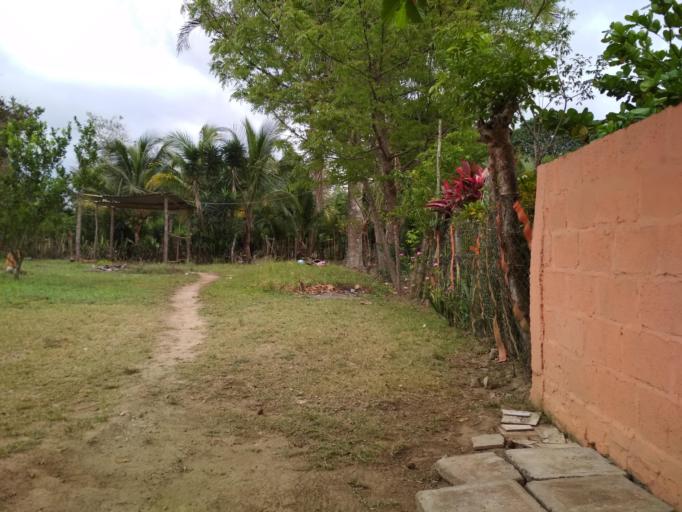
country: MX
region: Veracruz
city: El Tejar
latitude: 19.0634
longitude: -96.1530
